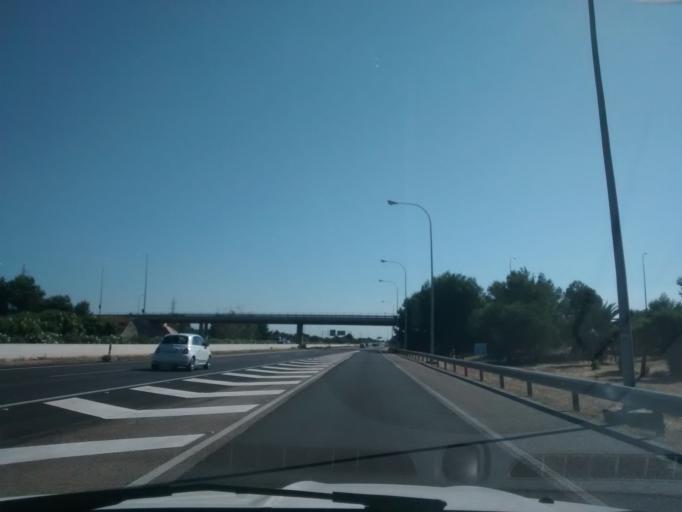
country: ES
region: Balearic Islands
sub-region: Illes Balears
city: Consell
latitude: 39.6690
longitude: 2.8245
